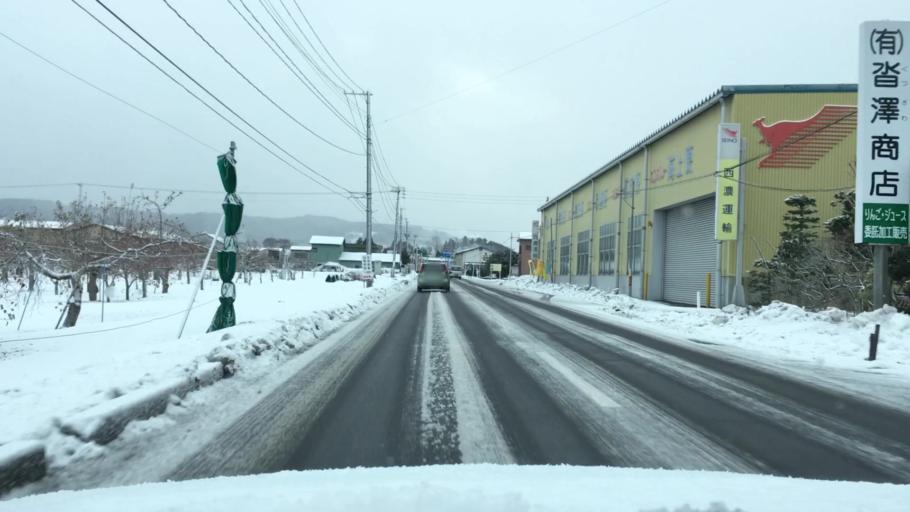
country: JP
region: Aomori
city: Hirosaki
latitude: 40.5580
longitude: 140.5342
